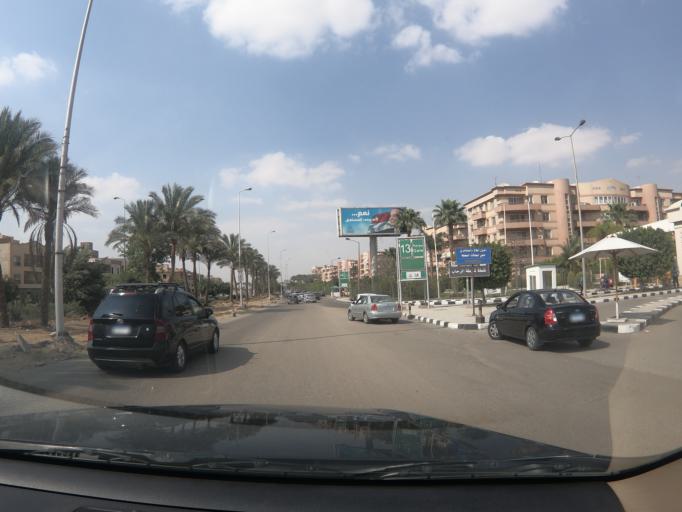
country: EG
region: Muhafazat al Qalyubiyah
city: Al Khankah
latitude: 30.0654
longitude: 31.4752
